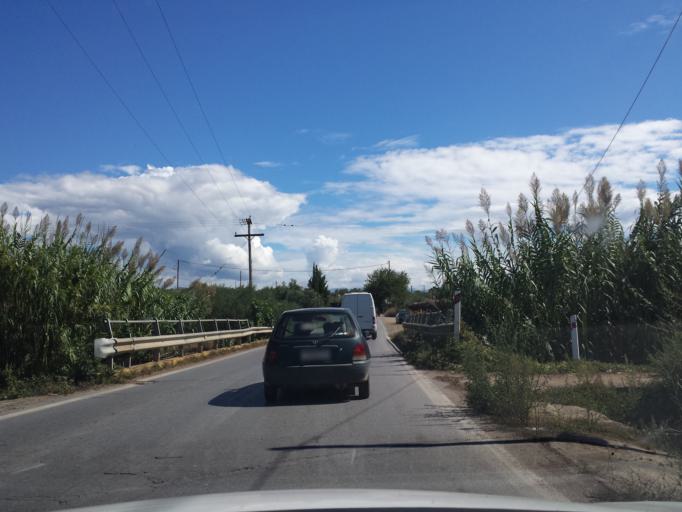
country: GR
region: Peloponnese
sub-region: Nomos Messinias
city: Messini
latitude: 37.0059
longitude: 21.9486
